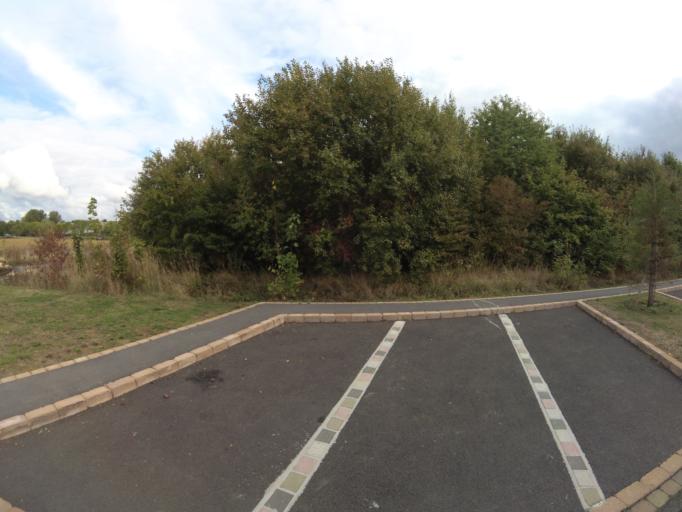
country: FR
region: Ile-de-France
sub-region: Departement de Seine-et-Marne
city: Chessy
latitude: 48.8723
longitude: 2.7665
